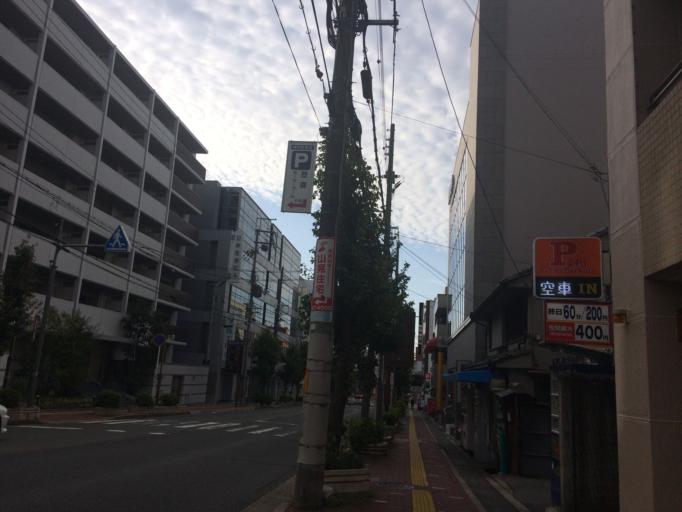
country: JP
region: Nara
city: Nara-shi
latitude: 34.6833
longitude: 135.8261
